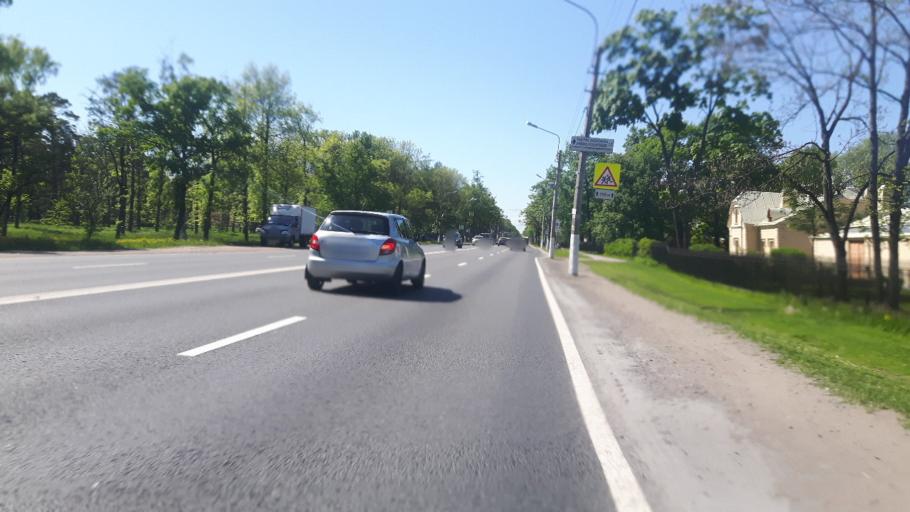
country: RU
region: St.-Petersburg
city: Peterhof
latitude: 59.8769
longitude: 29.9311
